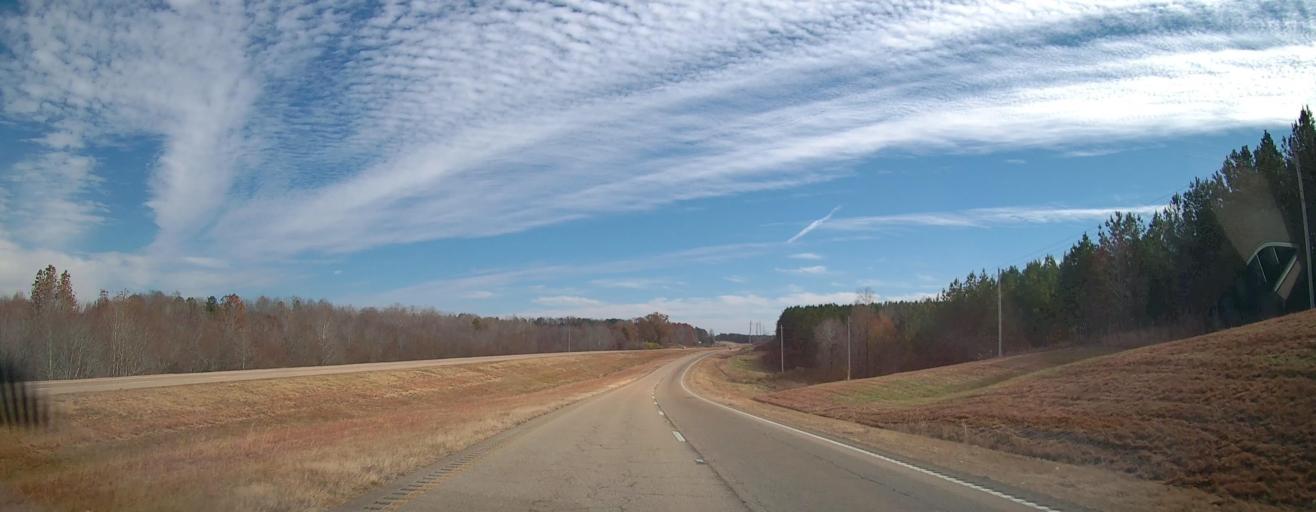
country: US
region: Mississippi
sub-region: Alcorn County
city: Corinth
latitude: 34.9362
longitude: -88.7311
